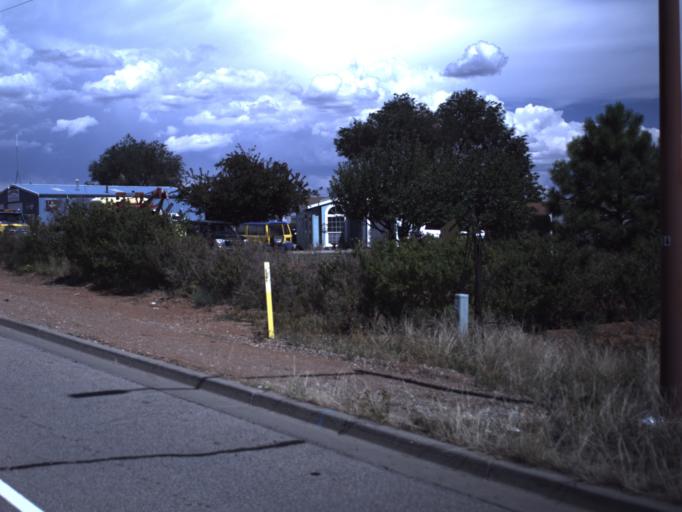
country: US
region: Utah
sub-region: San Juan County
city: Blanding
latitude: 37.5969
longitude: -109.4785
